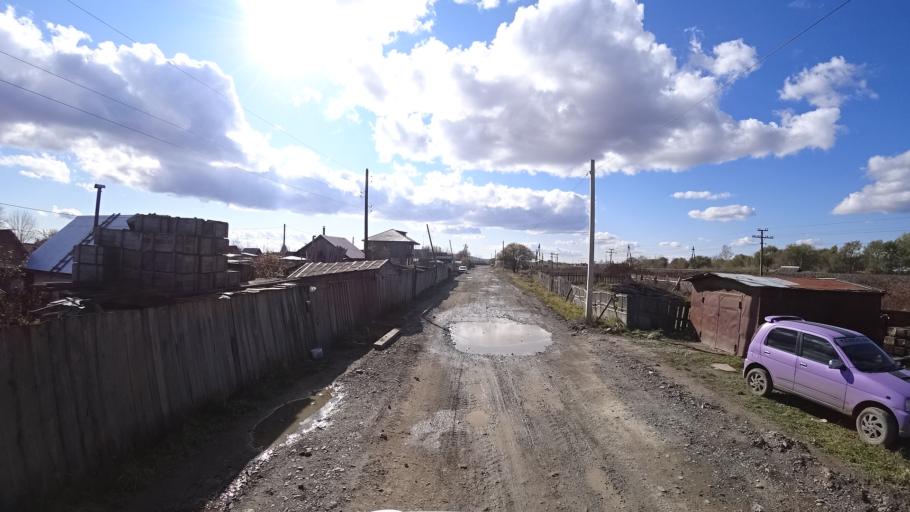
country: RU
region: Khabarovsk Krai
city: Amursk
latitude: 50.0948
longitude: 136.5039
